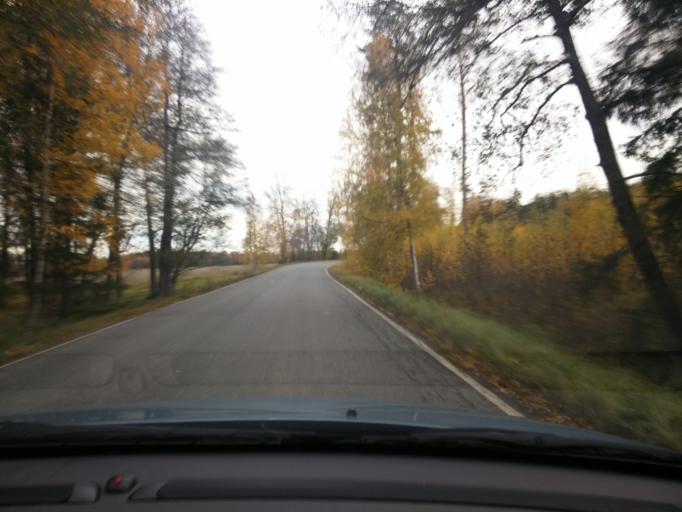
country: FI
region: Haeme
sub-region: Forssa
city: Tammela
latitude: 60.7917
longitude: 23.8190
